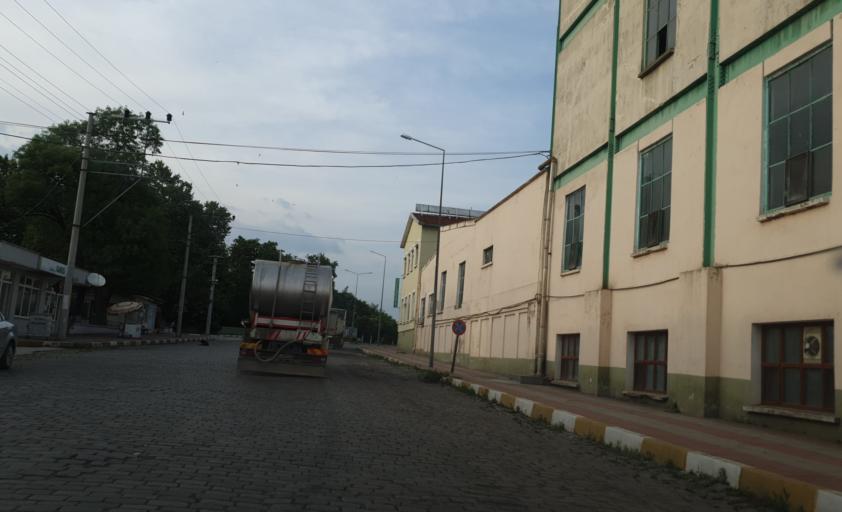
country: TR
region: Kirklareli
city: Babaeski
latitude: 41.3666
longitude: 27.1427
